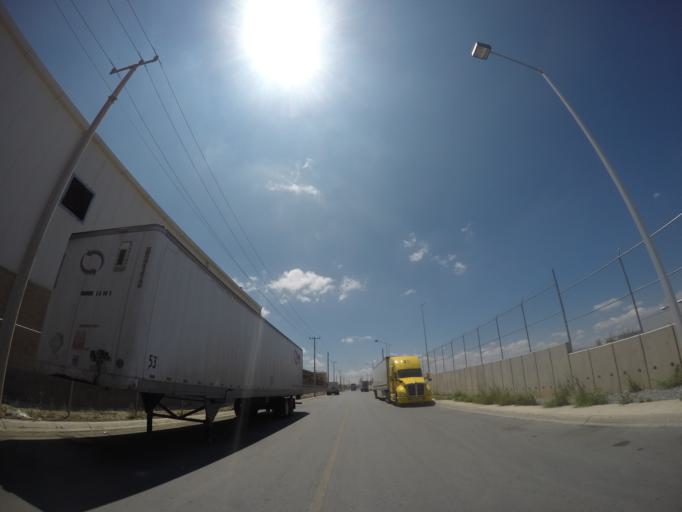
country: MX
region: San Luis Potosi
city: La Pila
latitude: 21.9744
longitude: -100.8780
